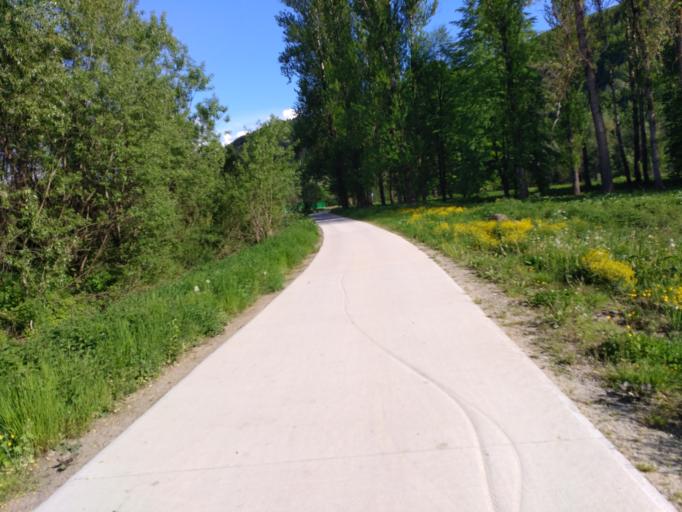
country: PL
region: Lesser Poland Voivodeship
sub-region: Powiat nowosadecki
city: Lacko
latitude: 49.5503
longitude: 20.4432
